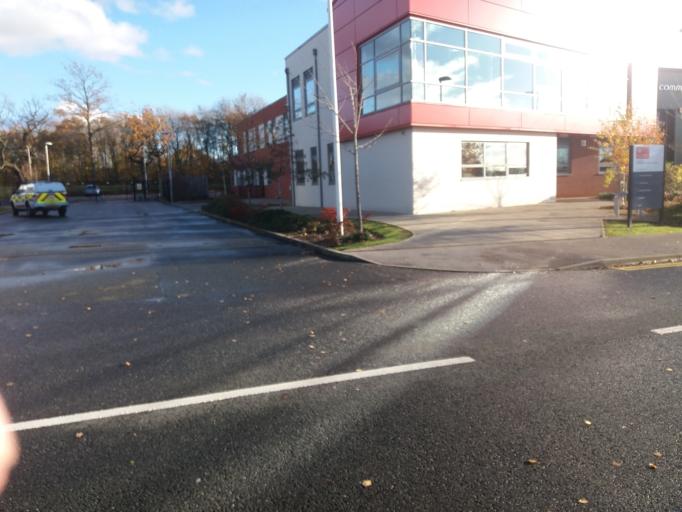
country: GB
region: England
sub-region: Lancashire
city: Euxton
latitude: 53.6625
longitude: -2.6565
